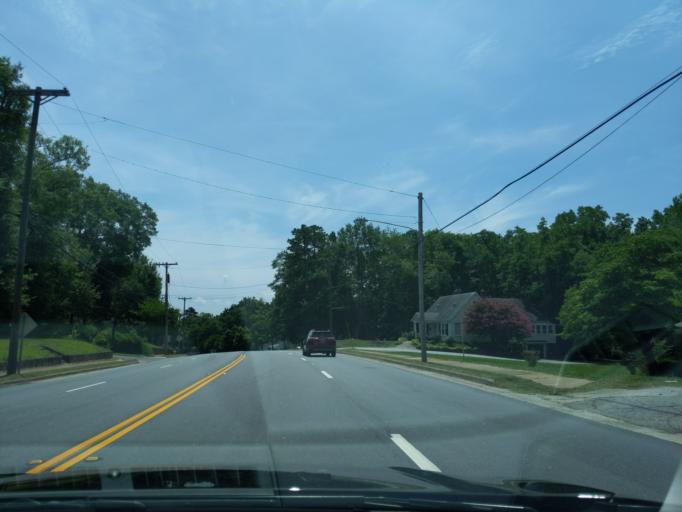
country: US
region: South Carolina
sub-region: Laurens County
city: Laurens
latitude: 34.5123
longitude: -82.0326
